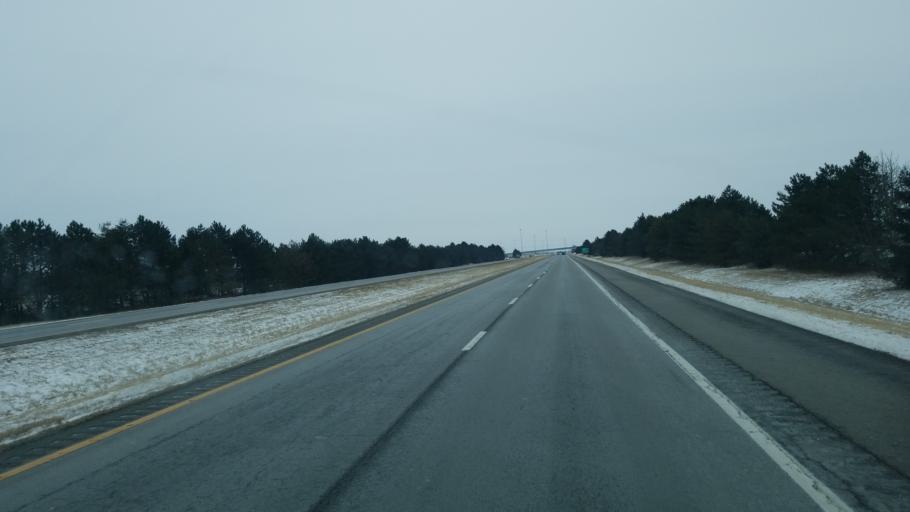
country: US
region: Ohio
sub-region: Wyandot County
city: Upper Sandusky
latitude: 40.8689
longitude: -83.3269
